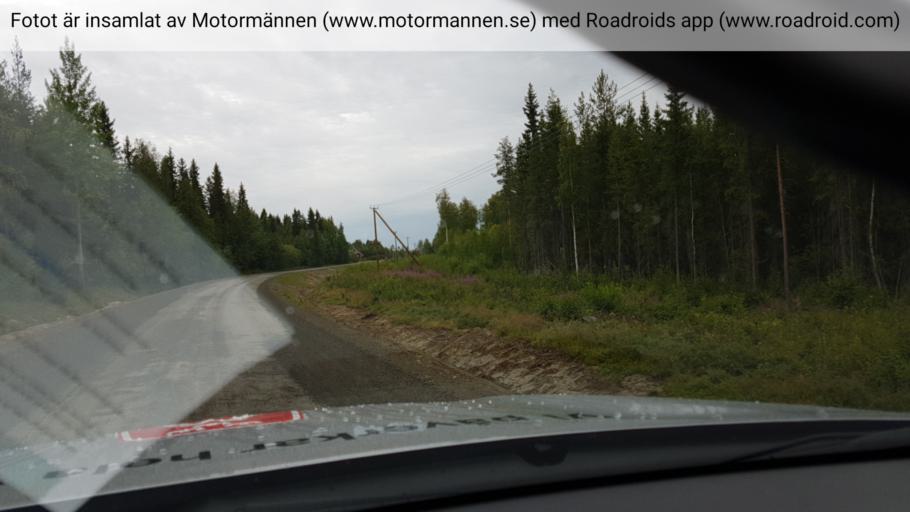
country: SE
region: Norrbotten
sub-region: Alvsbyns Kommun
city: AElvsbyn
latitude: 65.9166
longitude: 21.2703
